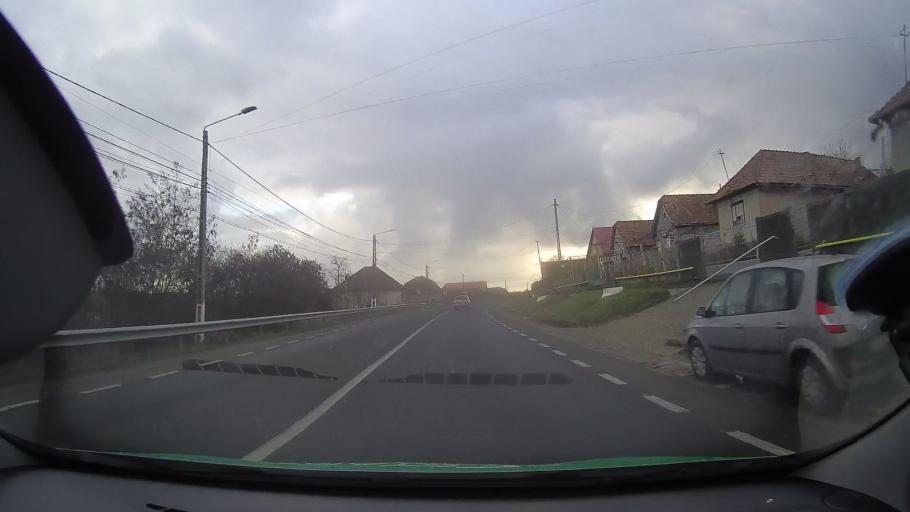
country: RO
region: Cluj
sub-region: Comuna Viisoara
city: Viisoara
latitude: 46.5093
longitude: 23.9187
